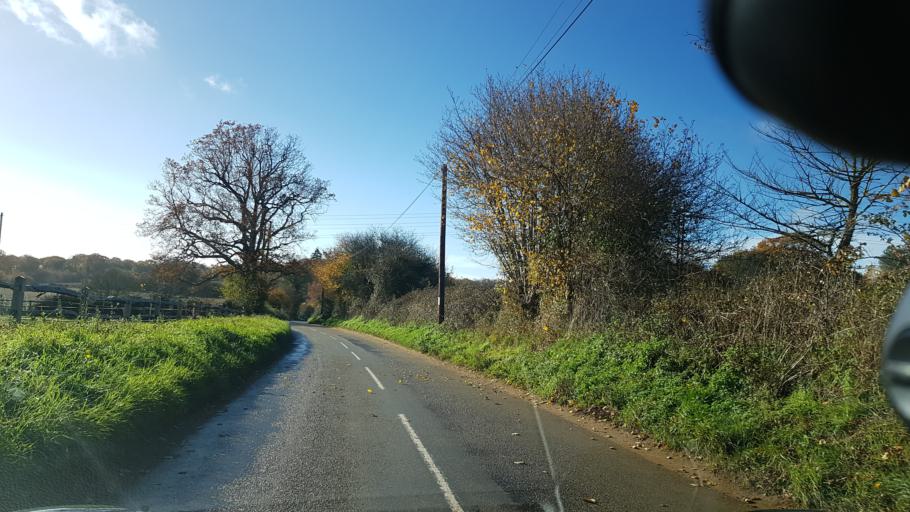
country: GB
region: England
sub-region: Surrey
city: Normandy
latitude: 51.2173
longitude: -0.6726
